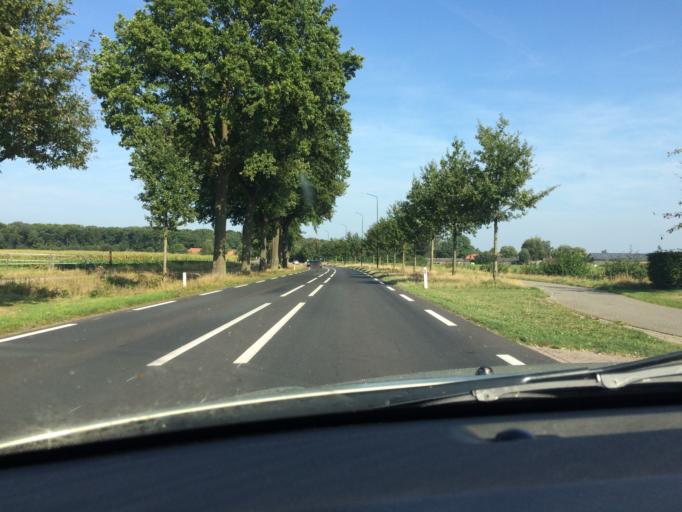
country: NL
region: North Brabant
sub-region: Gemeente Baarle-Nassau
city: Baarle-Nassau
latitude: 51.4597
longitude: 4.9452
